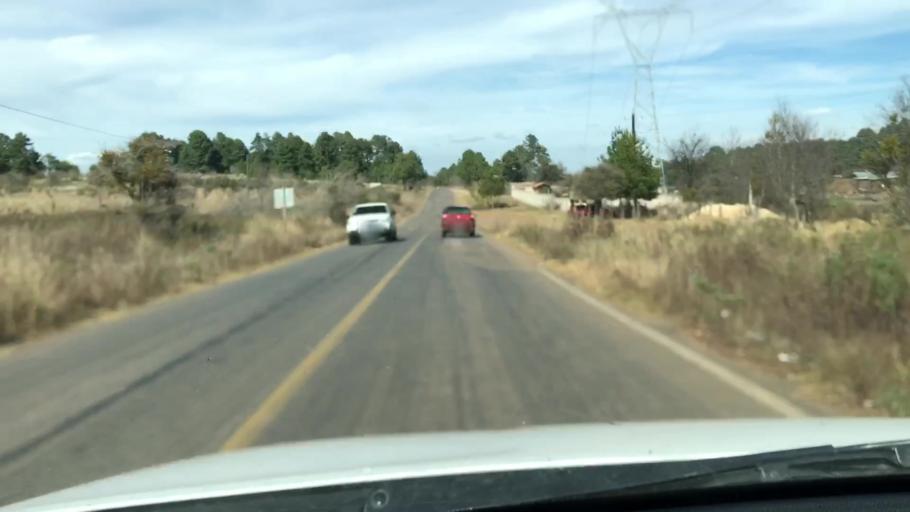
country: MX
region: Jalisco
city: Chiquilistlan
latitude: 20.1082
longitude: -103.7181
